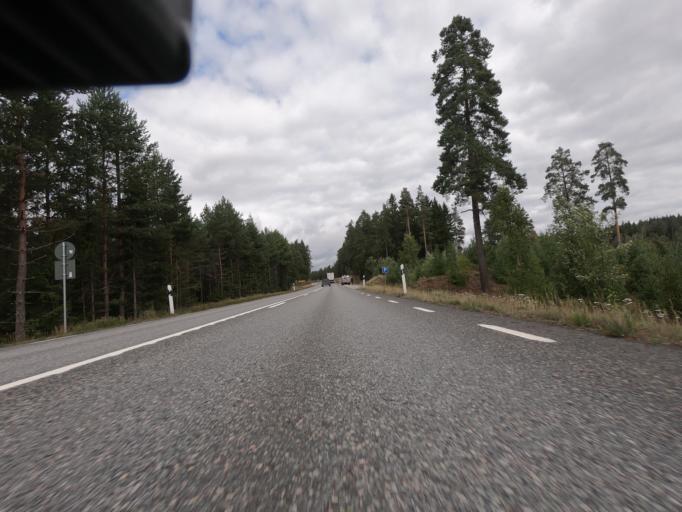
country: SE
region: Joenkoeping
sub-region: Vaggeryds Kommun
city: Vaggeryd
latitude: 57.4927
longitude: 14.2956
